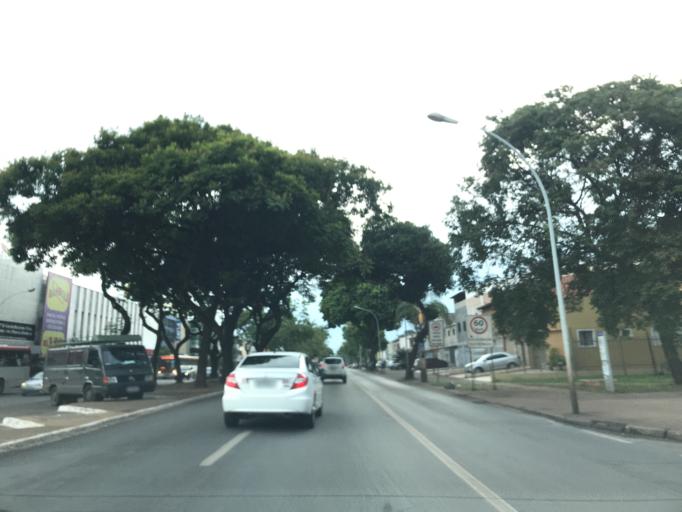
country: BR
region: Federal District
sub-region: Brasilia
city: Brasilia
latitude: -15.8039
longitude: -47.8968
